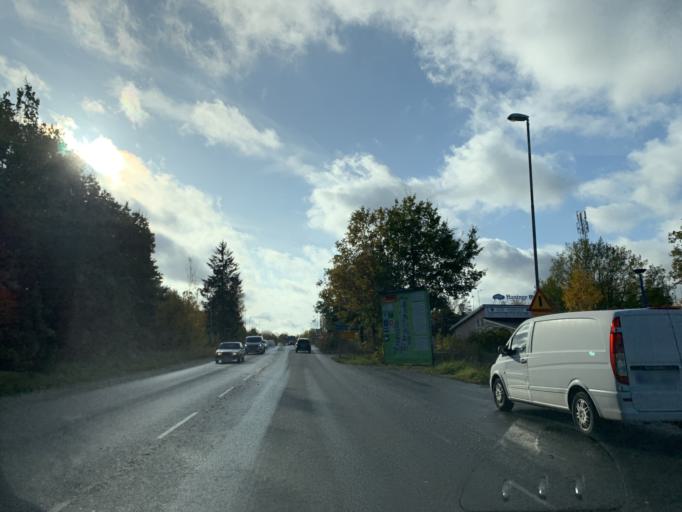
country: SE
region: Stockholm
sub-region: Haninge Kommun
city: Haninge
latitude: 59.1788
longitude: 18.1631
